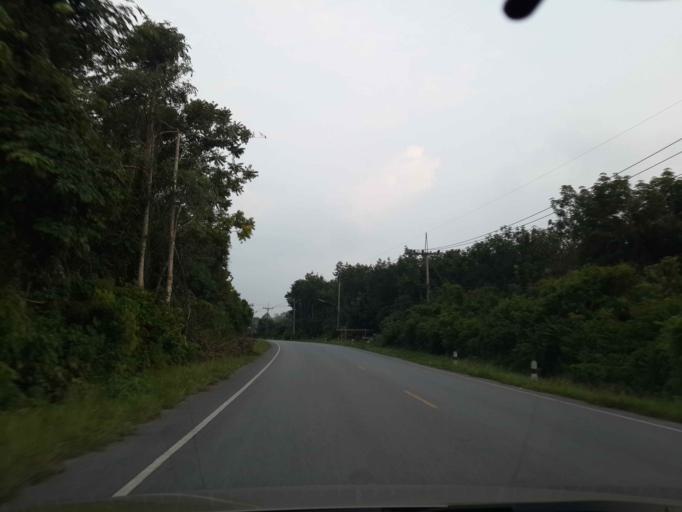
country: TH
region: Narathiwat
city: Rueso
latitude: 6.3684
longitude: 101.4639
